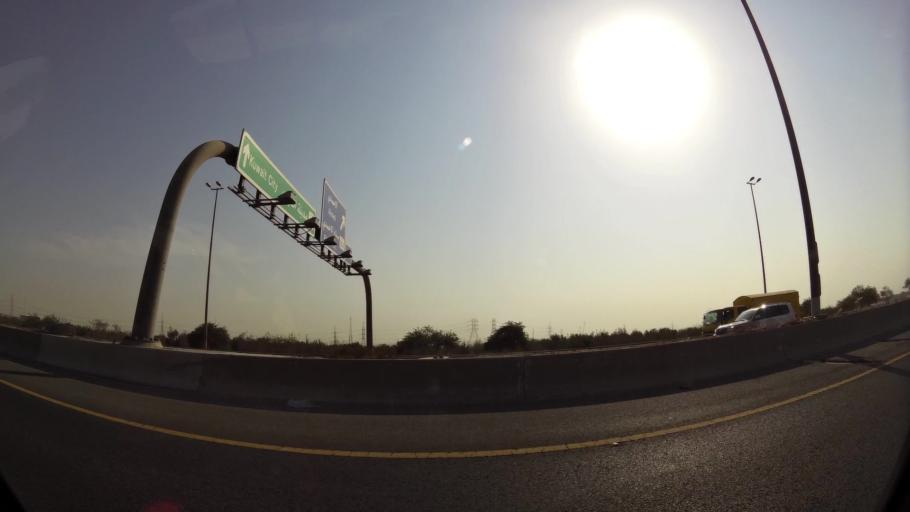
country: KW
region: Al Ahmadi
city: Al Ahmadi
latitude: 29.0582
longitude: 48.0971
